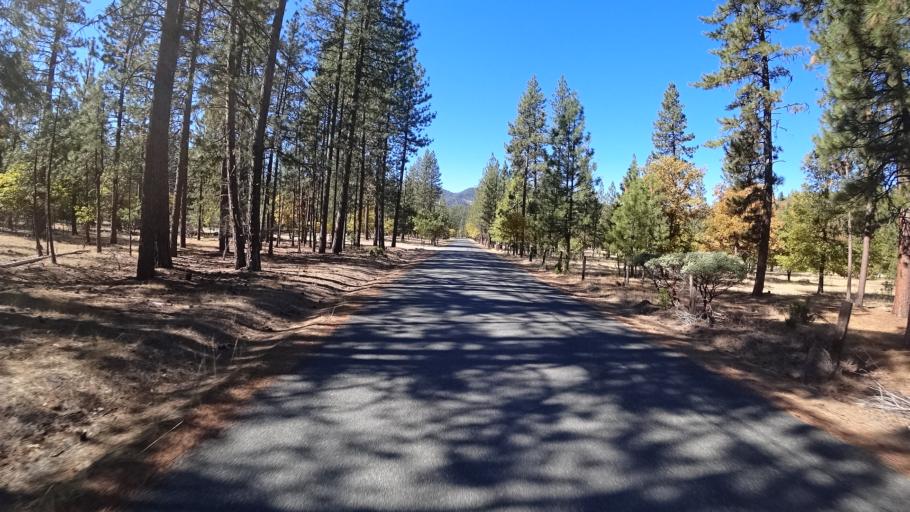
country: US
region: California
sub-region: Siskiyou County
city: Yreka
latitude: 41.5411
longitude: -122.9421
